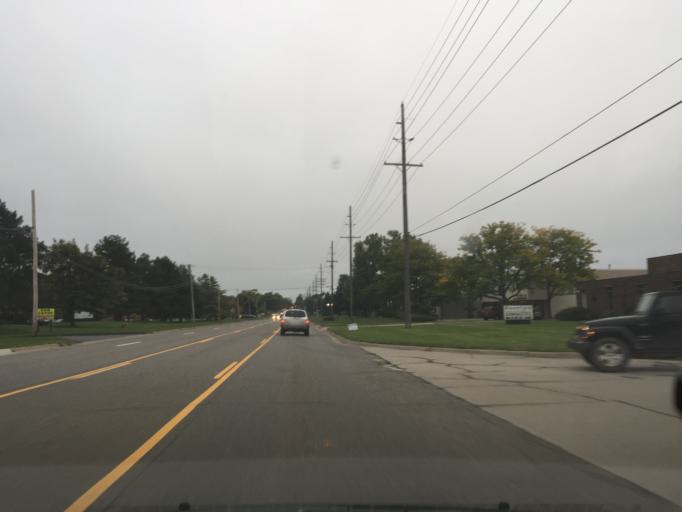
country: US
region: Michigan
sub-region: Oakland County
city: Pontiac
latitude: 42.6080
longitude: -83.2877
